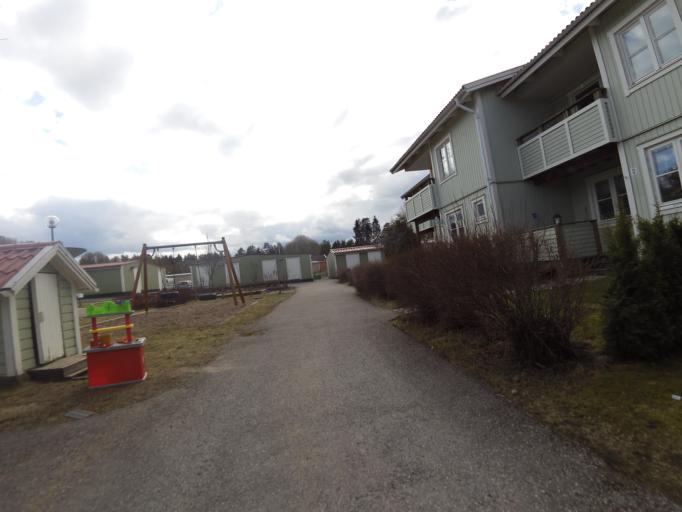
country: SE
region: Gaevleborg
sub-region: Gavle Kommun
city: Gavle
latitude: 60.6950
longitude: 17.0919
